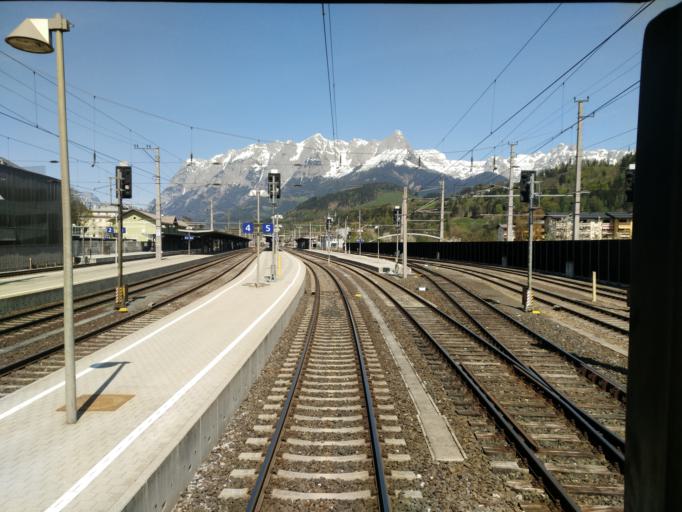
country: AT
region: Salzburg
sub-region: Politischer Bezirk Sankt Johann im Pongau
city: Bischofshofen
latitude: 47.4158
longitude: 13.2203
